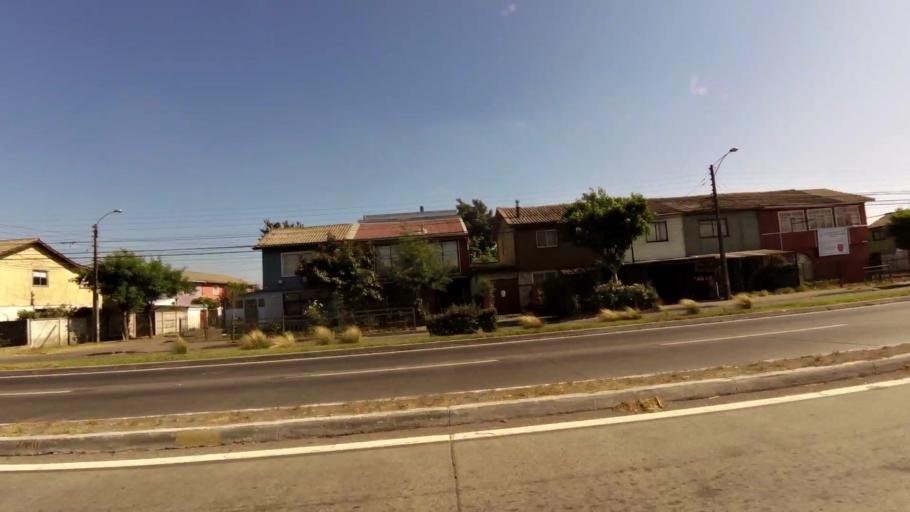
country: CL
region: Biobio
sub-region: Provincia de Concepcion
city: Talcahuano
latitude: -36.7799
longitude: -73.0981
